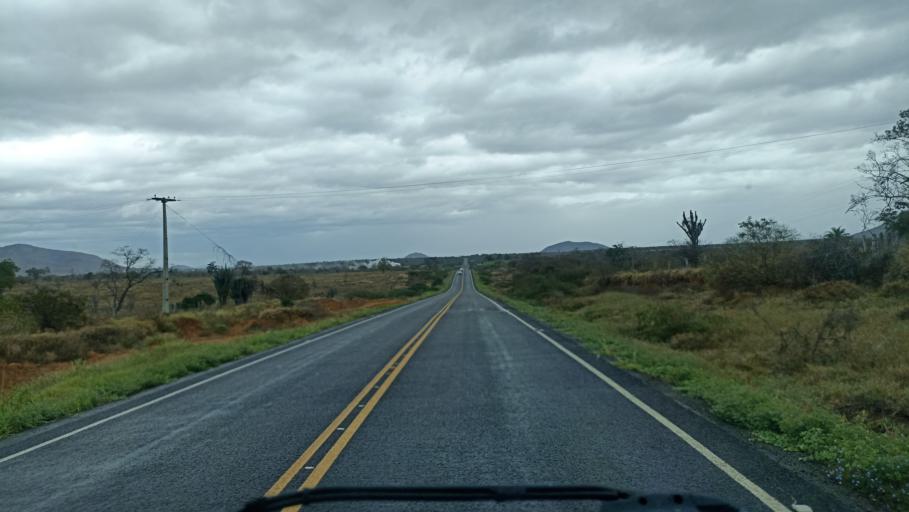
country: BR
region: Bahia
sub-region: Iacu
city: Iacu
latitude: -12.9674
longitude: -40.4930
